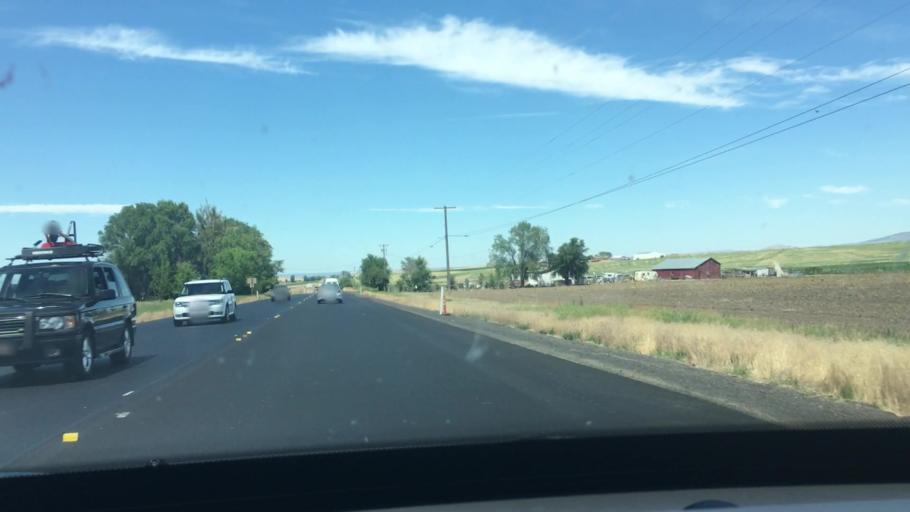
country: US
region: Oregon
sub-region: Jefferson County
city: Culver
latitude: 44.5076
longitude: -121.1873
